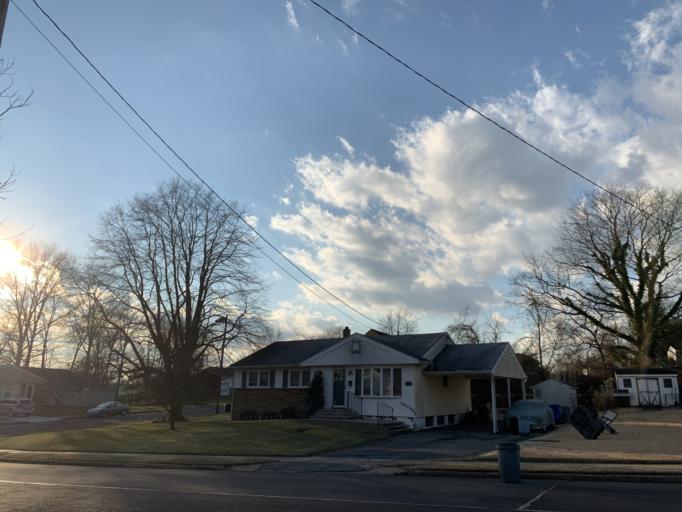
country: US
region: New Jersey
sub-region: Burlington County
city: Mount Holly
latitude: 40.0041
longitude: -74.8005
